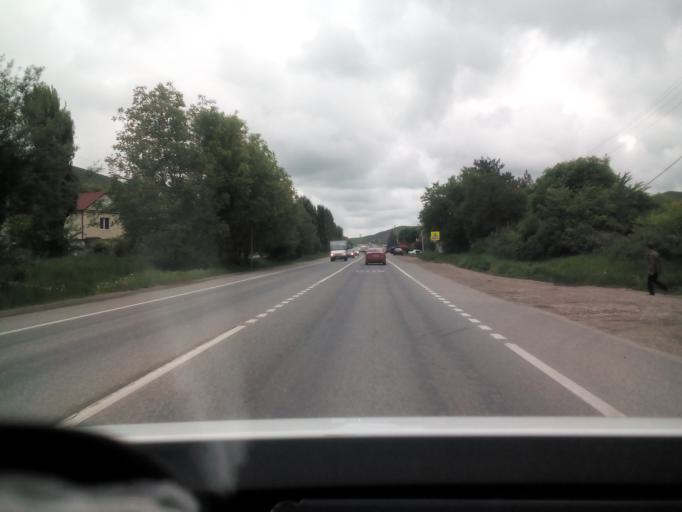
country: RU
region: Stavropol'skiy
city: Yasnaya Polyana
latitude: 43.9699
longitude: 42.7818
